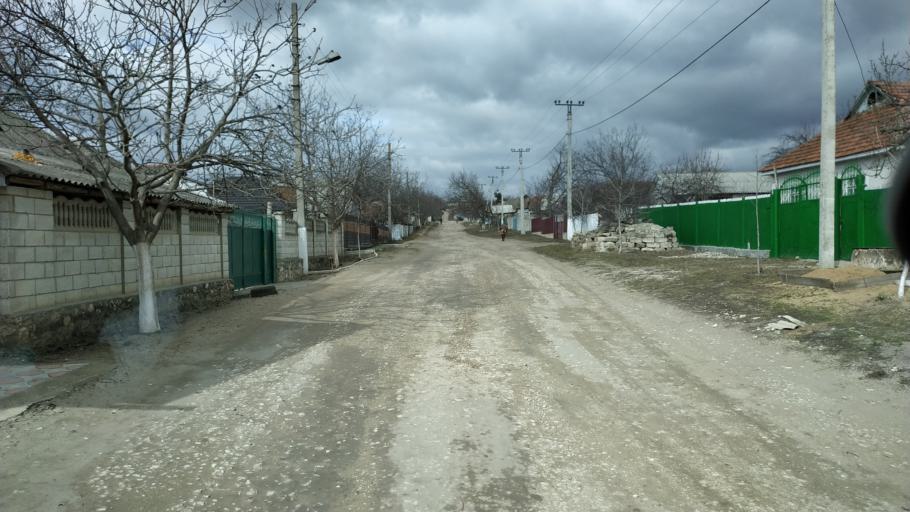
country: MD
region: Stinga Nistrului
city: Bucovat
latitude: 47.2248
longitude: 28.4416
